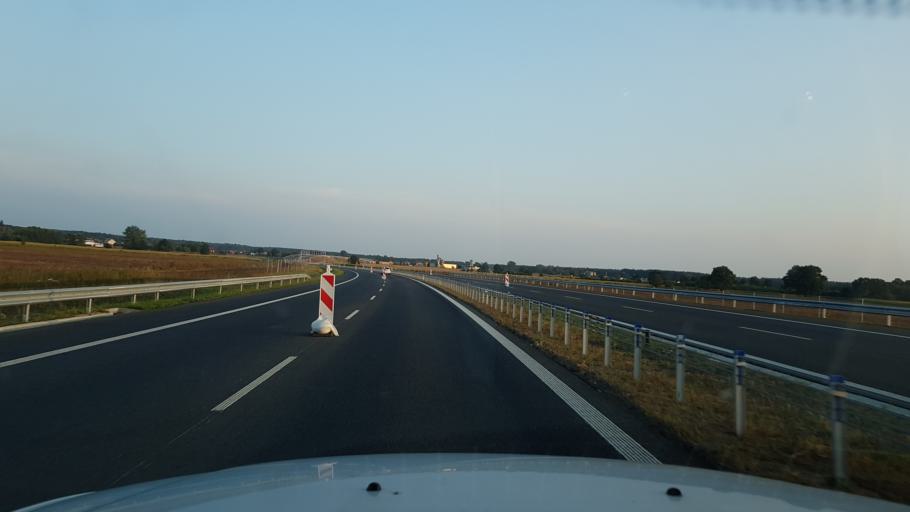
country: PL
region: West Pomeranian Voivodeship
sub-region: Powiat gryficki
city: Ploty
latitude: 53.8079
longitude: 15.2477
